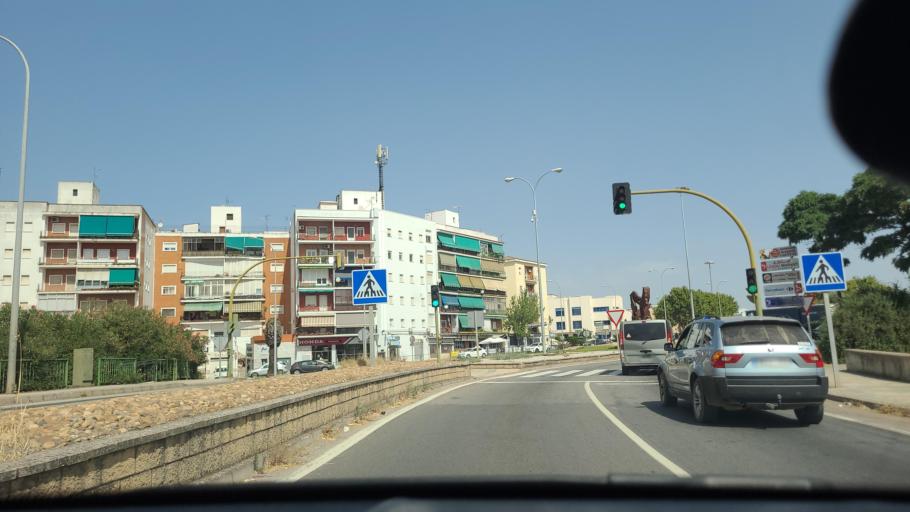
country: ES
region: Extremadura
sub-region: Provincia de Badajoz
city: Zafra
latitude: 38.4233
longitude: -6.4116
